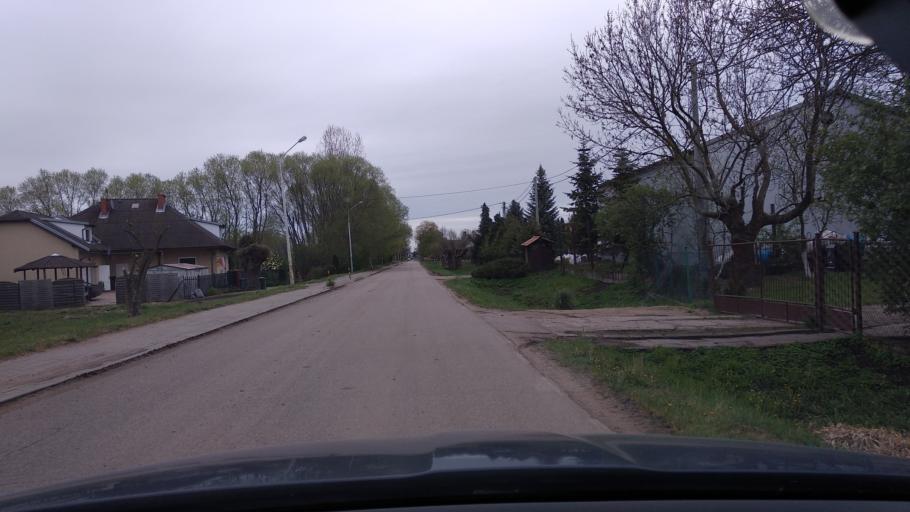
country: PL
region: Pomeranian Voivodeship
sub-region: Powiat gdanski
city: Pruszcz Gdanski
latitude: 54.2761
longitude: 18.6731
